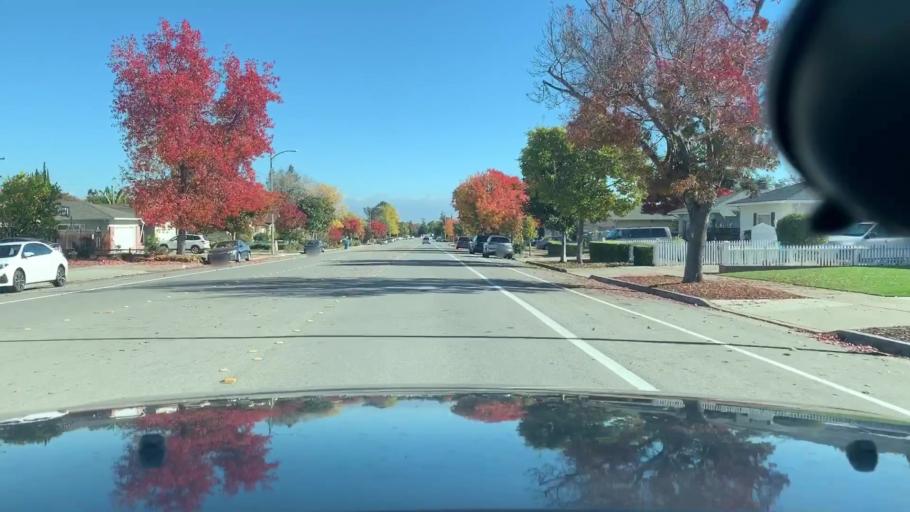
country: US
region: California
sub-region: Santa Clara County
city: Cupertino
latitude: 37.3006
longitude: -122.0389
